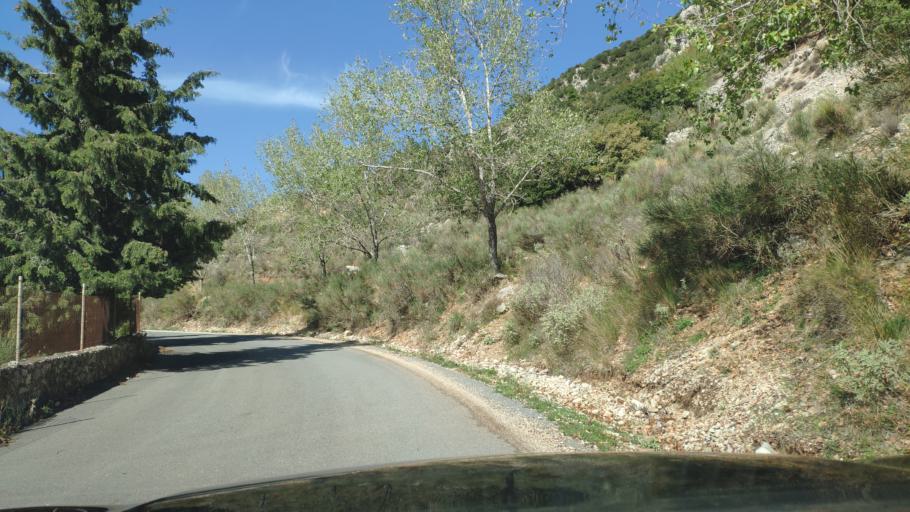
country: GR
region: Peloponnese
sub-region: Nomos Arkadias
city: Dimitsana
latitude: 37.5854
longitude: 22.0467
